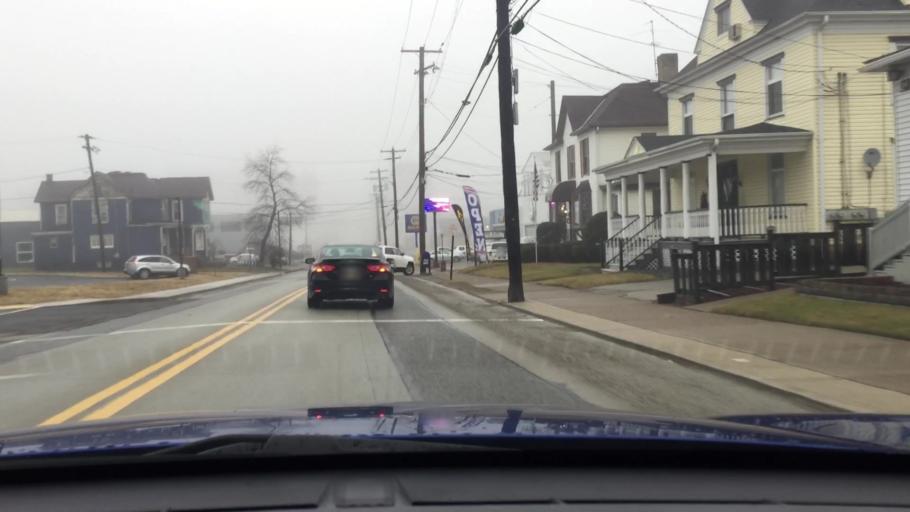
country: US
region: Pennsylvania
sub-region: Washington County
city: Canonsburg
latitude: 40.2558
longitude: -80.1855
